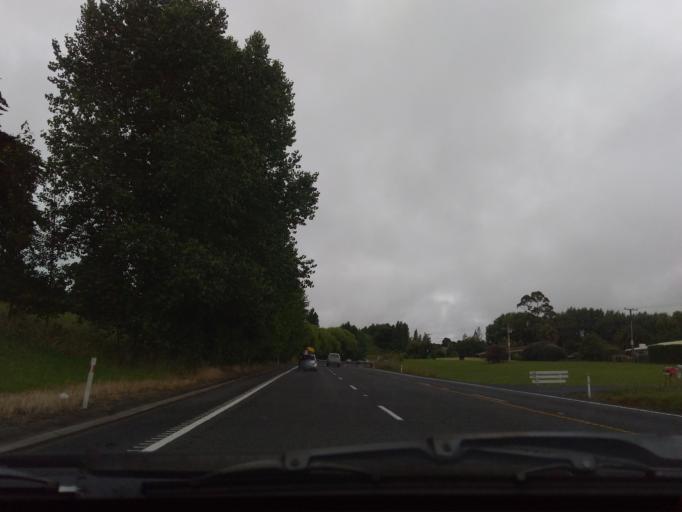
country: NZ
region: Auckland
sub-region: Auckland
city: Wellsford
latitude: -36.1545
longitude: 174.4397
